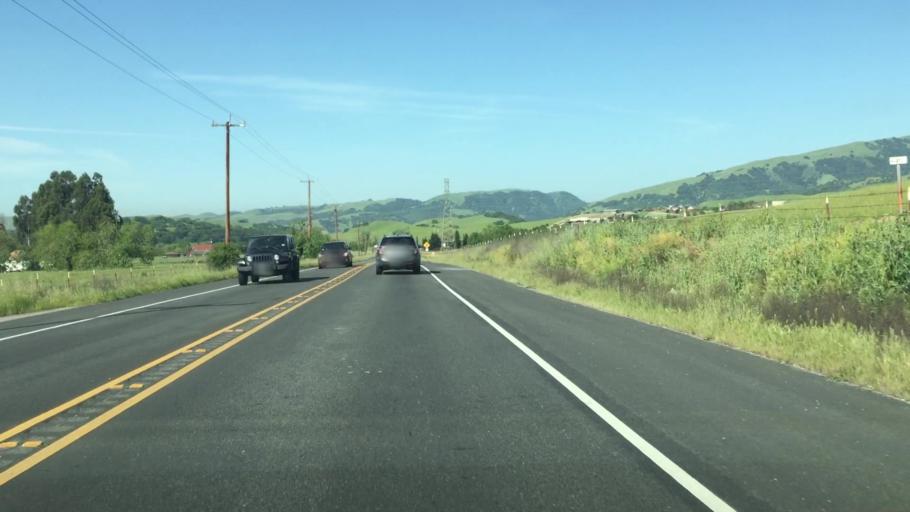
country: US
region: California
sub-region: Alameda County
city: Pleasanton
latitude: 37.6053
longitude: -121.8369
